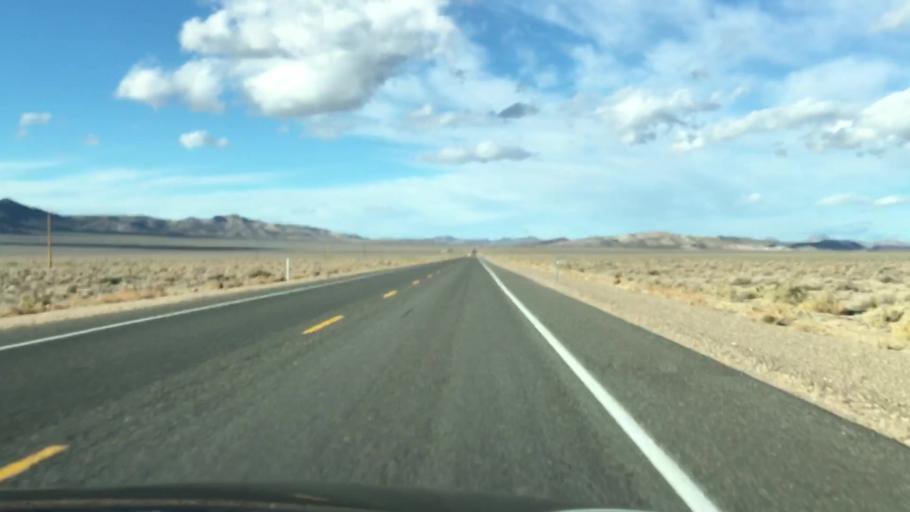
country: US
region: Nevada
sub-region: Esmeralda County
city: Goldfield
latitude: 37.4737
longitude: -117.1770
